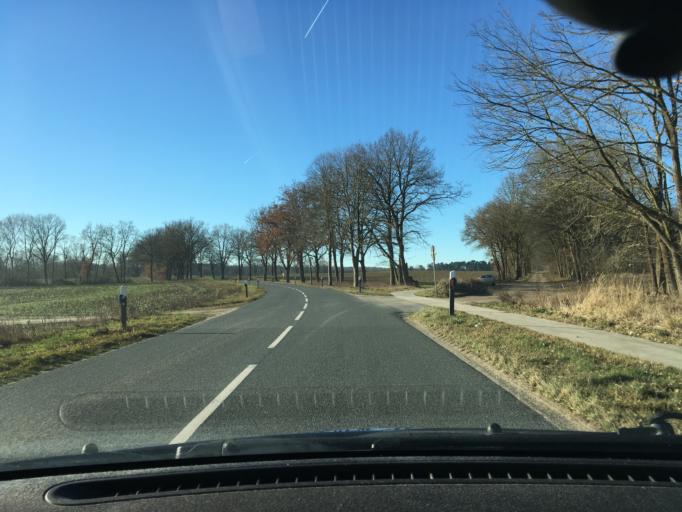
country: DE
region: Lower Saxony
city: Melbeck
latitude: 53.1759
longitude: 10.3831
